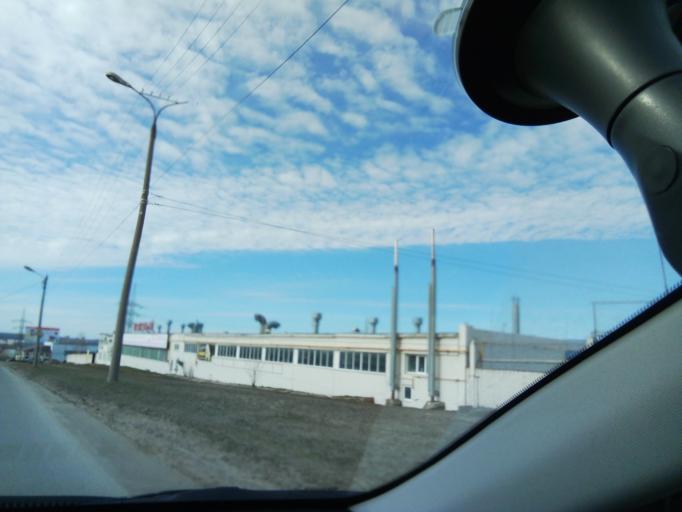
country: RU
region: Chuvashia
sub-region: Cheboksarskiy Rayon
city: Cheboksary
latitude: 56.0992
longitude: 47.2549
